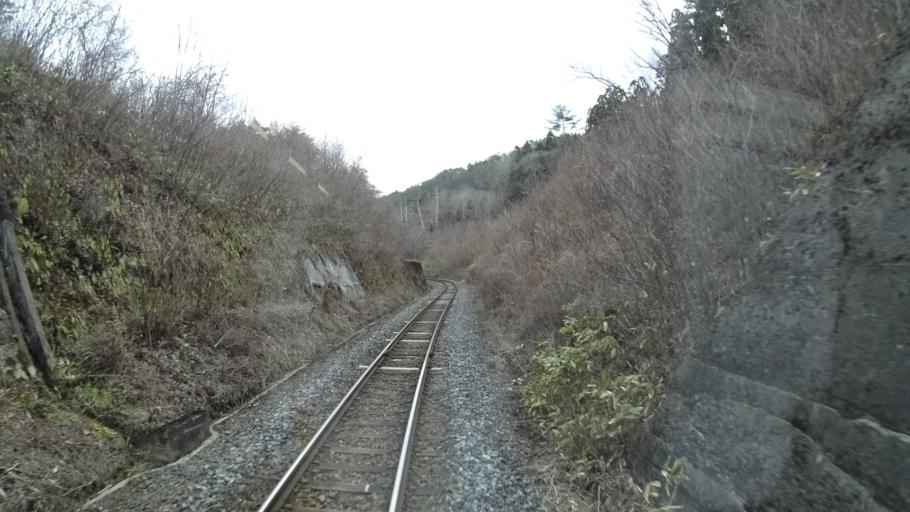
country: JP
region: Iwate
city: Tono
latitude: 39.3245
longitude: 141.3658
